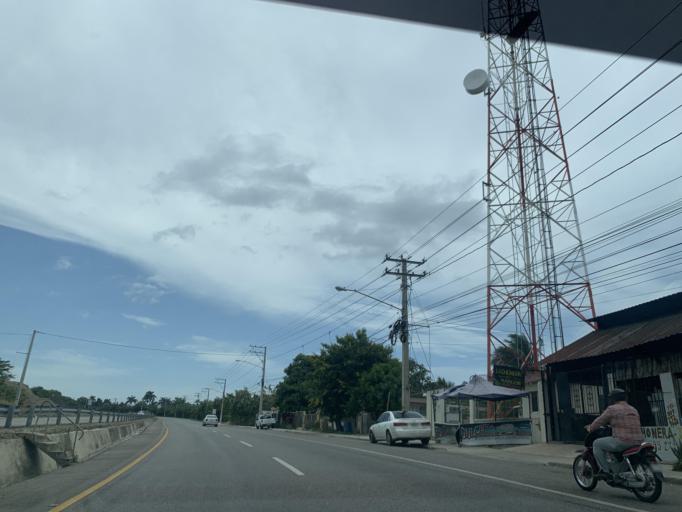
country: DO
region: Puerto Plata
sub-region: Puerto Plata
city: Puerto Plata
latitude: 19.8269
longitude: -70.7484
